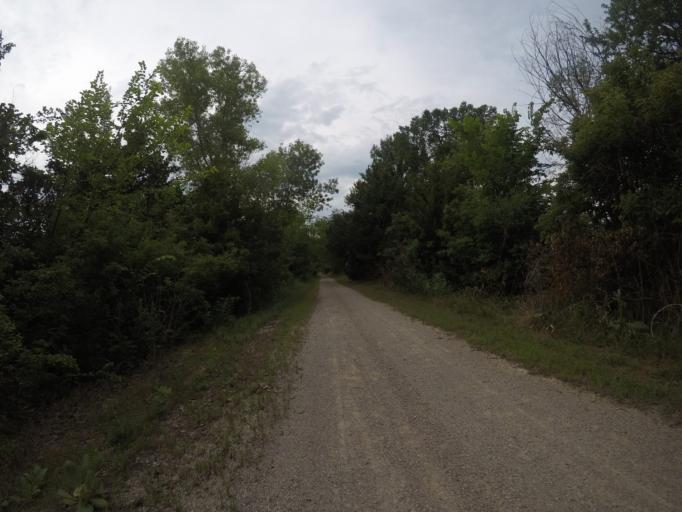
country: US
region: Kansas
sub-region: Franklin County
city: Ottawa
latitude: 38.4733
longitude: -95.2740
